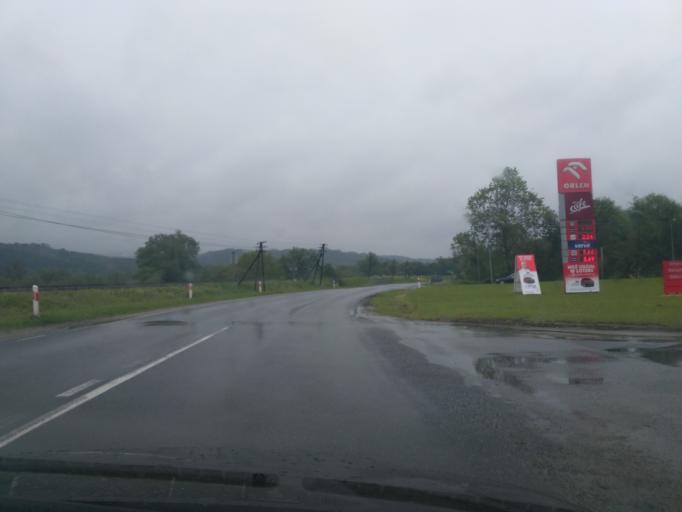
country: PL
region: Subcarpathian Voivodeship
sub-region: Powiat strzyzowski
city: Frysztak
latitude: 49.8209
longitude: 21.6271
